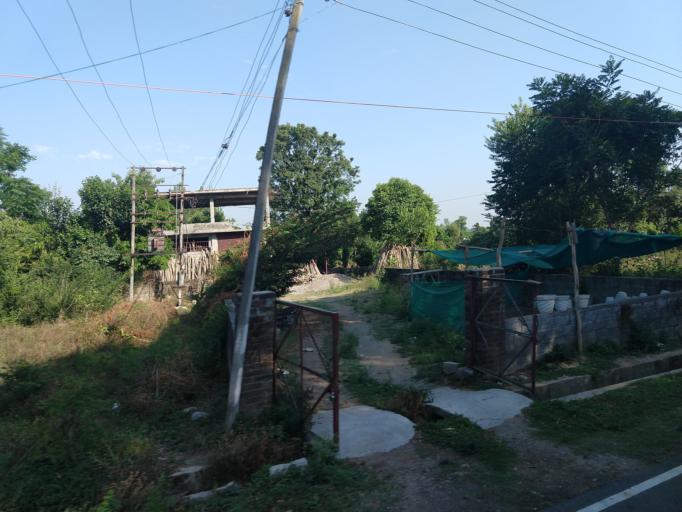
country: IN
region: Himachal Pradesh
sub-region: Chamba
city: Chowari
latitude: 32.3501
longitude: 75.9125
